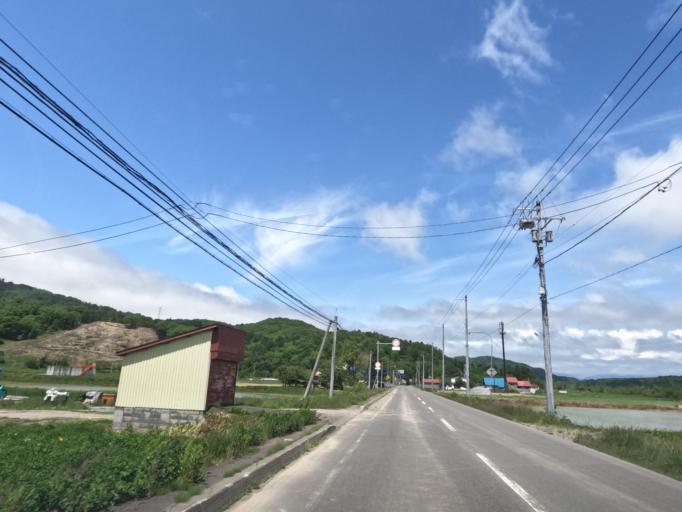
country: JP
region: Hokkaido
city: Tobetsu
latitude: 43.2934
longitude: 141.5403
